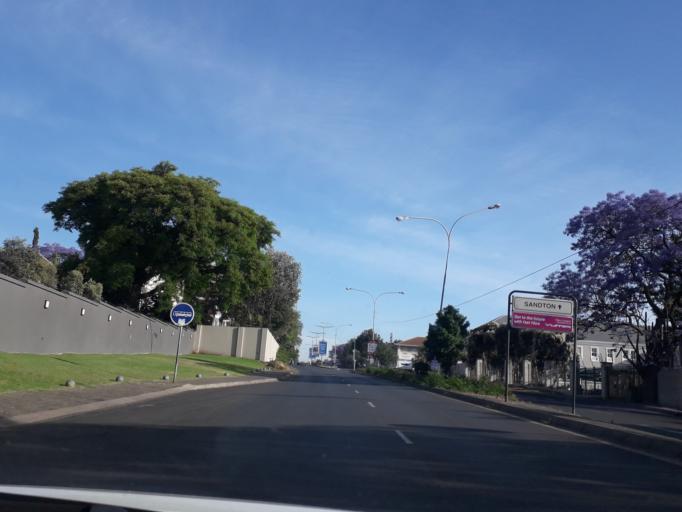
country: ZA
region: Gauteng
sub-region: City of Johannesburg Metropolitan Municipality
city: Johannesburg
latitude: -26.1272
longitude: 28.0494
